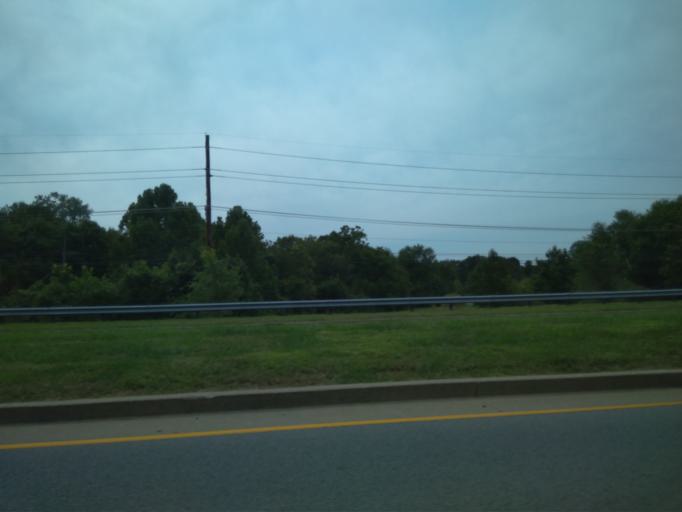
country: US
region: Kentucky
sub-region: Jefferson County
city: Anchorage
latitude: 38.2784
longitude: -85.5653
